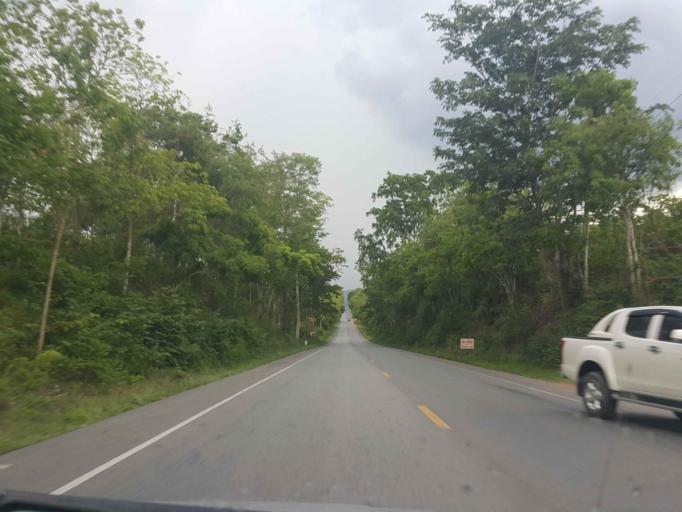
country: TH
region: Phrae
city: Den Chai
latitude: 17.9680
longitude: 100.0495
